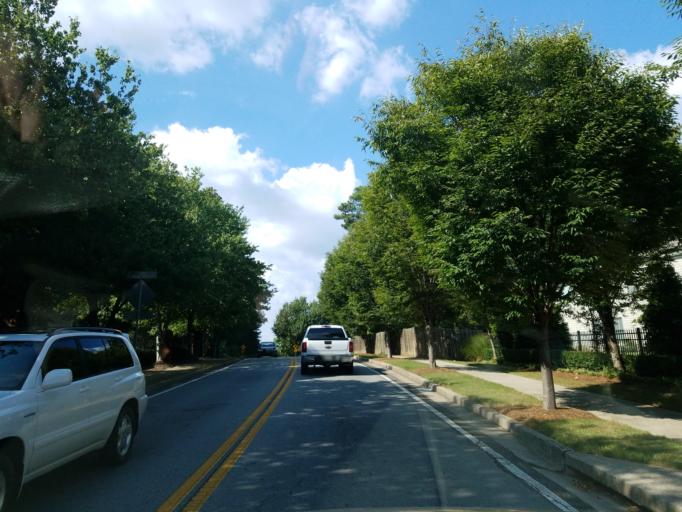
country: US
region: Georgia
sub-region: Fulton County
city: Roswell
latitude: 34.0208
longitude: -84.3306
